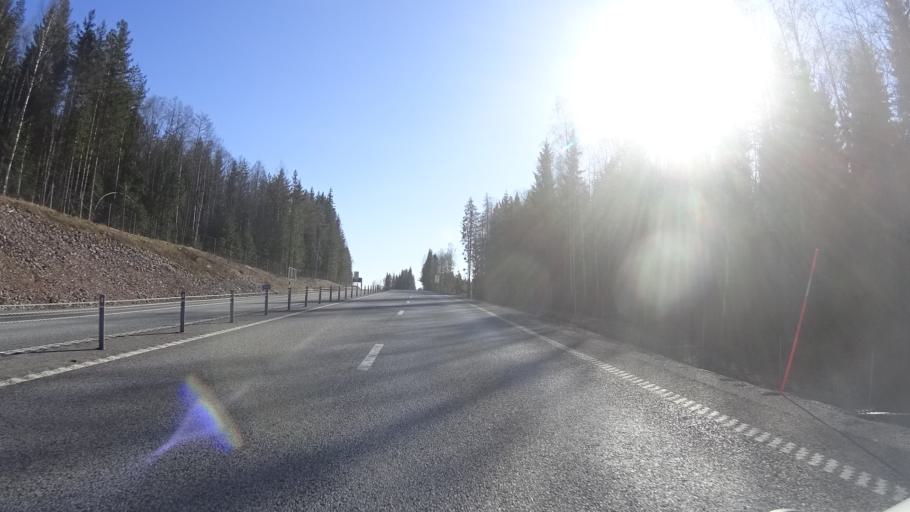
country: SE
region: Vaermland
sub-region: Arvika Kommun
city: Arvika
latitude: 59.6567
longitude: 12.7584
